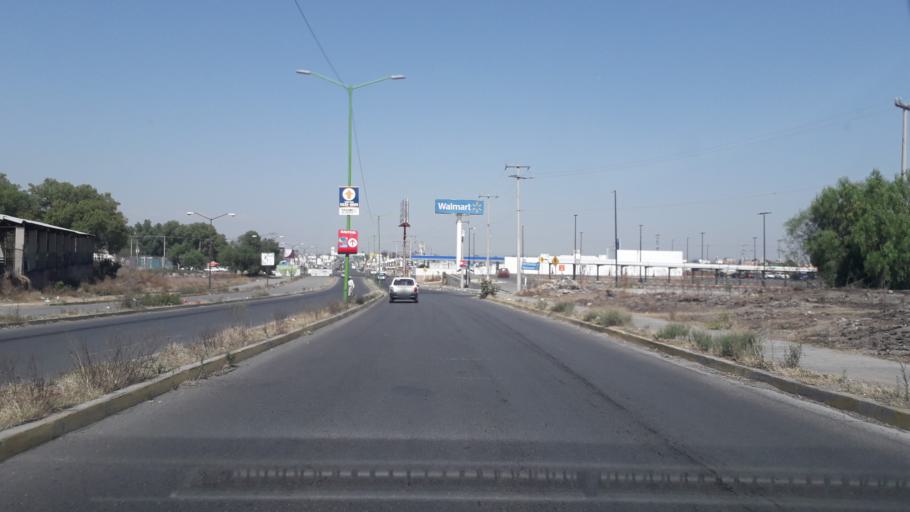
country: MX
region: Mexico
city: Santo Tomas Chiconautla
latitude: 19.6575
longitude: -99.0173
